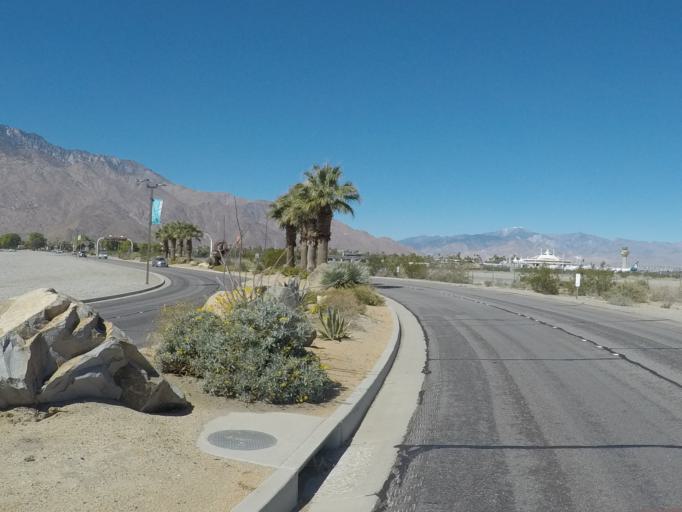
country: US
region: California
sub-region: Riverside County
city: Palm Springs
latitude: 33.8189
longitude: -116.5022
